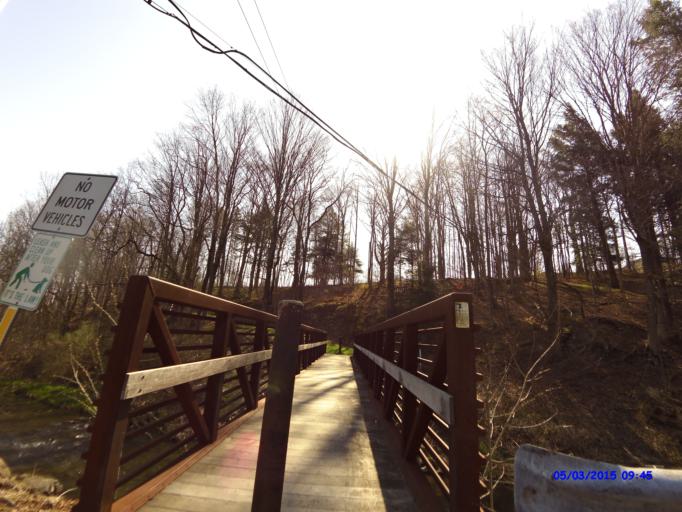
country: US
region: New York
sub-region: Cattaraugus County
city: Franklinville
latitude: 42.3322
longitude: -78.4577
